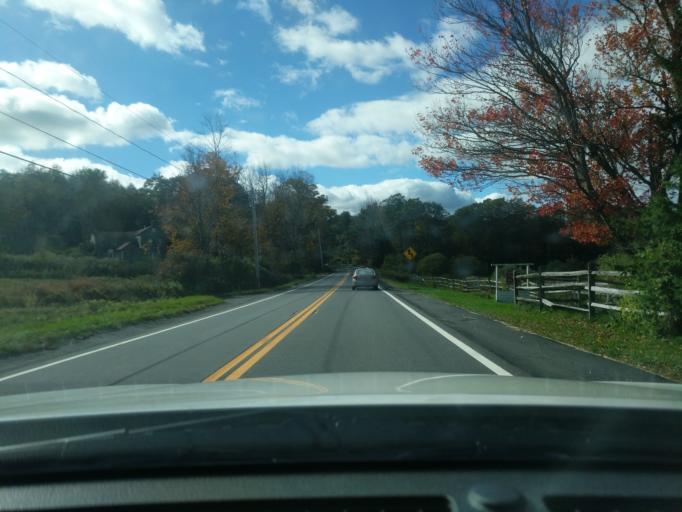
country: US
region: Massachusetts
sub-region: Berkshire County
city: Otis
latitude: 42.1925
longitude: -73.1347
